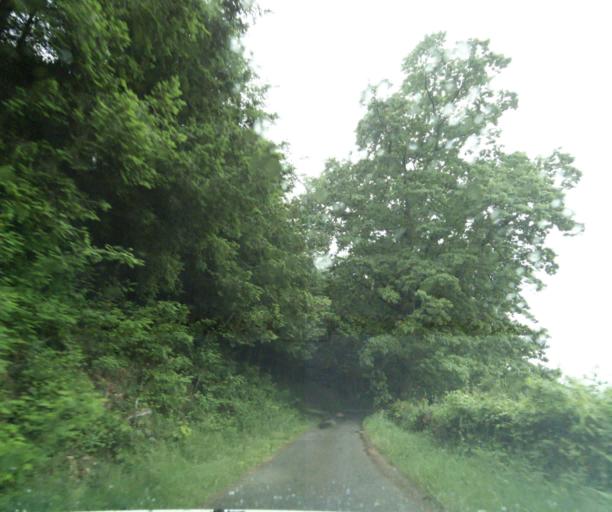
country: FR
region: Bourgogne
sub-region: Departement de Saone-et-Loire
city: La Clayette
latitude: 46.3517
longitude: 4.3641
